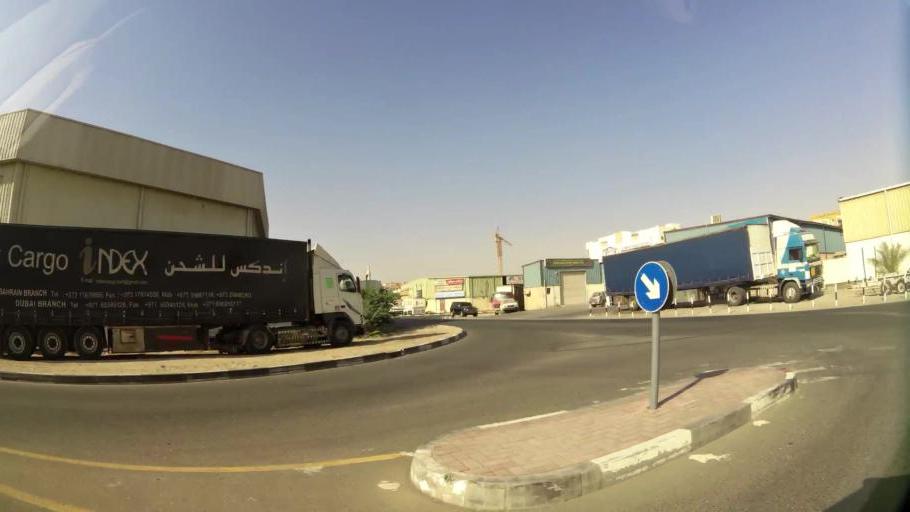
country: AE
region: Ash Shariqah
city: Sharjah
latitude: 25.2820
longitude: 55.3853
